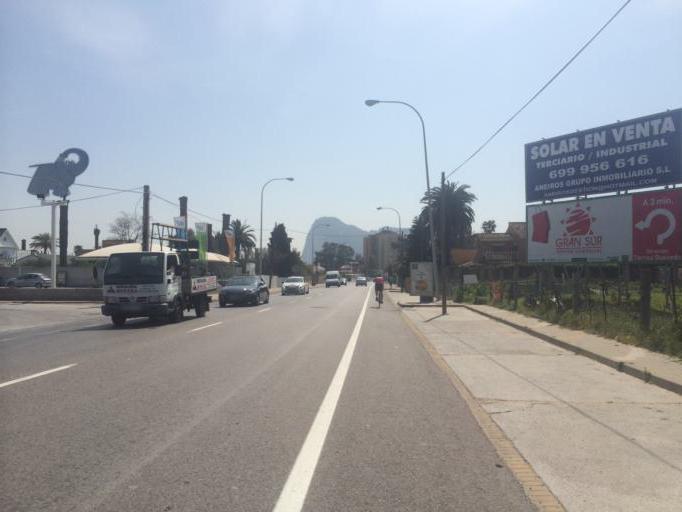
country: ES
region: Andalusia
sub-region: Provincia de Cadiz
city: La Linea de la Concepcion
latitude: 36.1736
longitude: -5.3730
